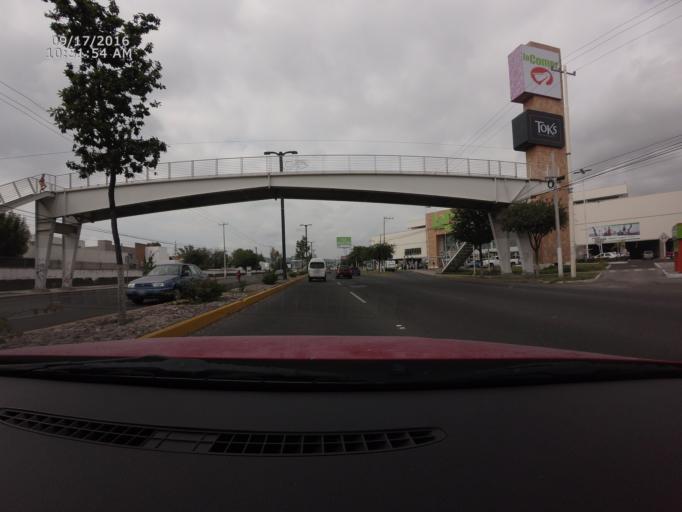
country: MX
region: Queretaro
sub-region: Corregidora
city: El Pueblito
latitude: 20.5440
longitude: -100.4295
